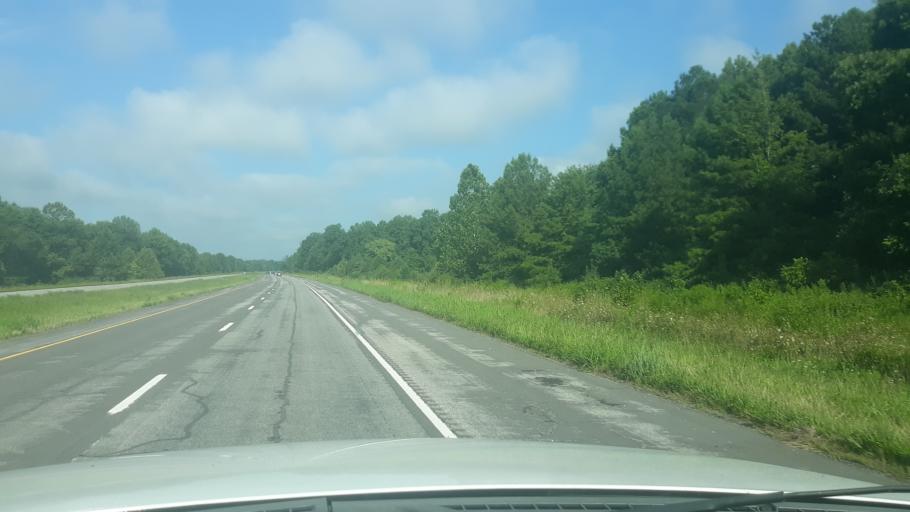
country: US
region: Illinois
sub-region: Saline County
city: Carrier Mills
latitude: 37.7342
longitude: -88.6809
